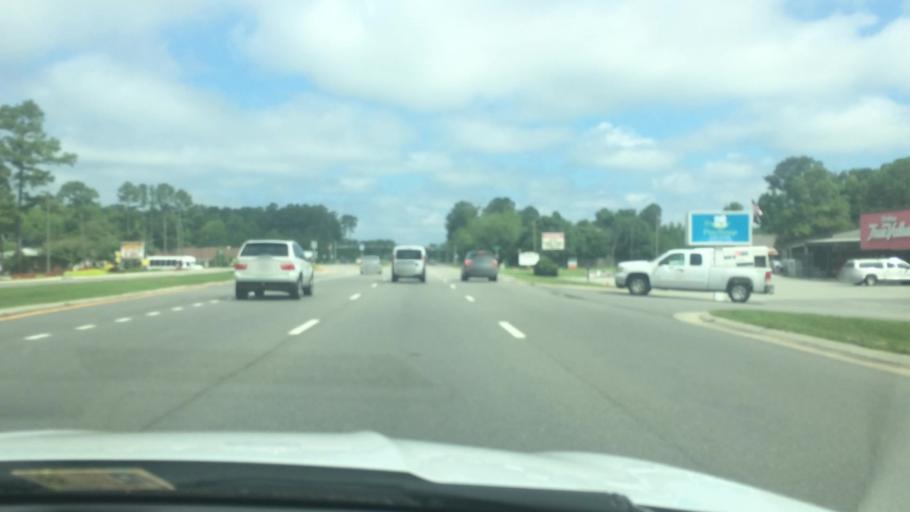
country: US
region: Virginia
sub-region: York County
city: Yorktown
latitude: 37.1528
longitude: -76.4608
